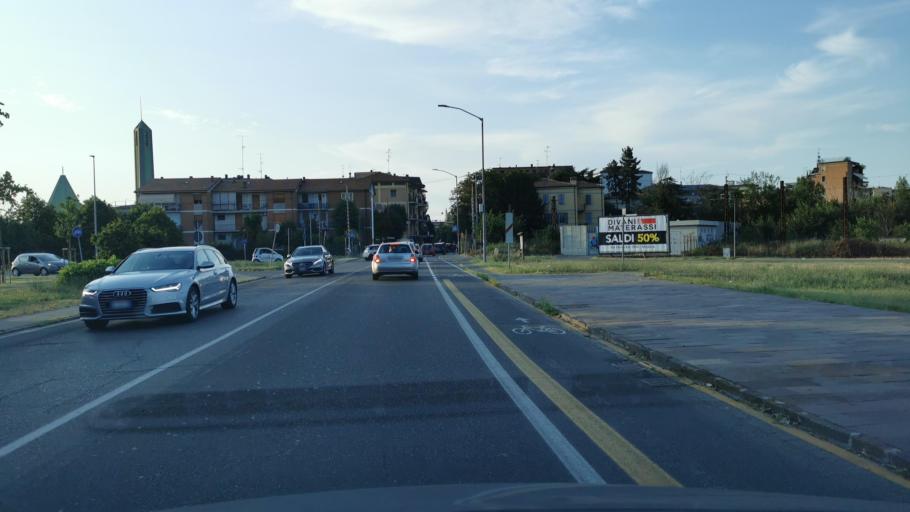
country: IT
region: Emilia-Romagna
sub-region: Provincia di Modena
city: Modena
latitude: 44.6321
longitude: 10.9263
